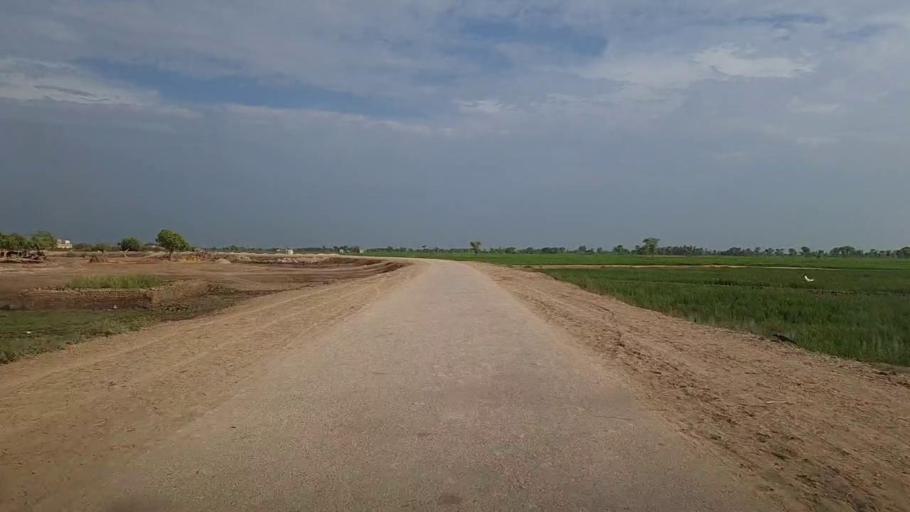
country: PK
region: Sindh
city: Thul
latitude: 28.2662
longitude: 68.8513
